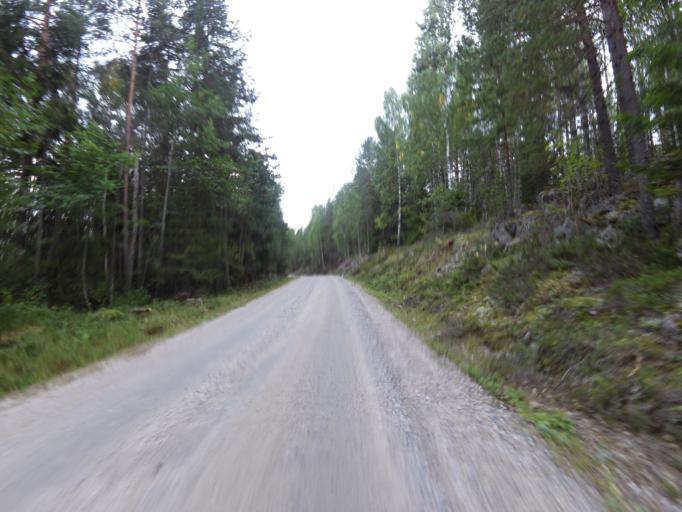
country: SE
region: Gaevleborg
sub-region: Sandvikens Kommun
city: Sandviken
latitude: 60.7569
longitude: 16.8597
